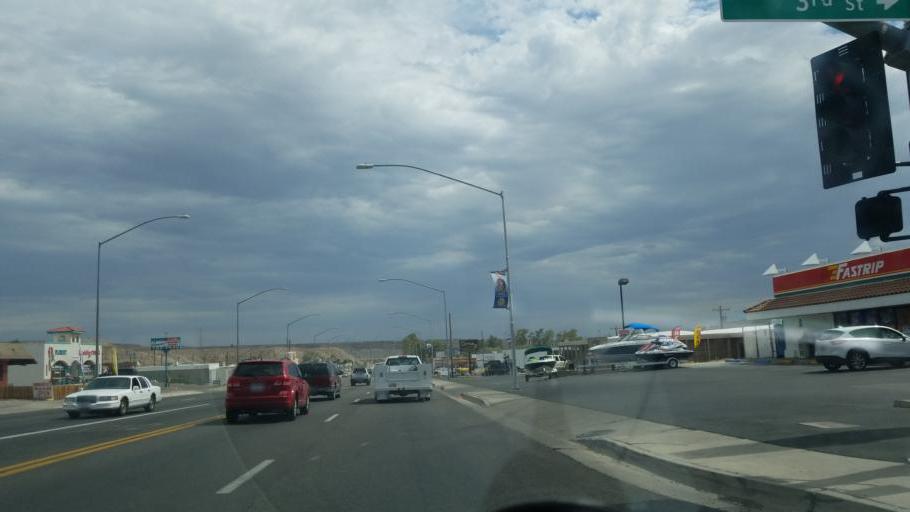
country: US
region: Arizona
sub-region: Mohave County
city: Bullhead City
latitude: 35.1459
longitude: -114.5689
